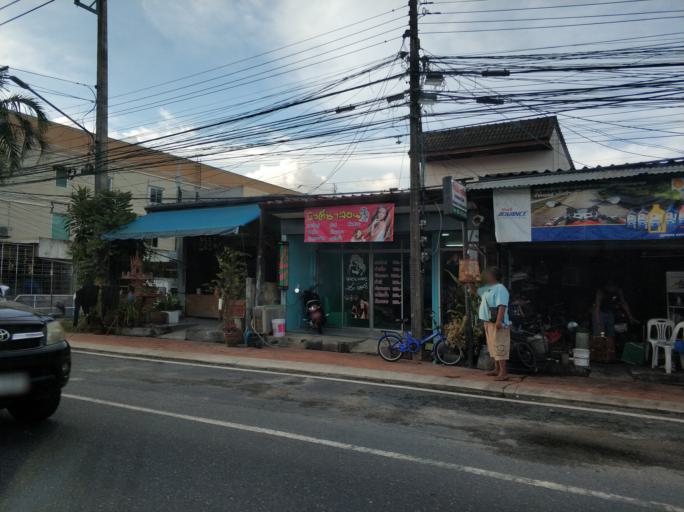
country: TH
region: Phuket
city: Kathu
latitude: 7.8999
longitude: 98.3486
